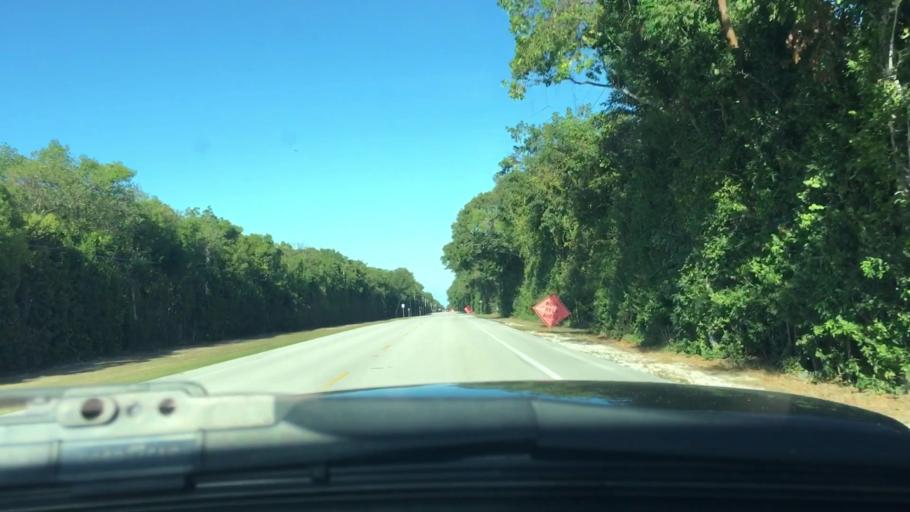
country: US
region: Florida
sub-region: Monroe County
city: North Key Largo
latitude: 25.1800
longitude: -80.3664
